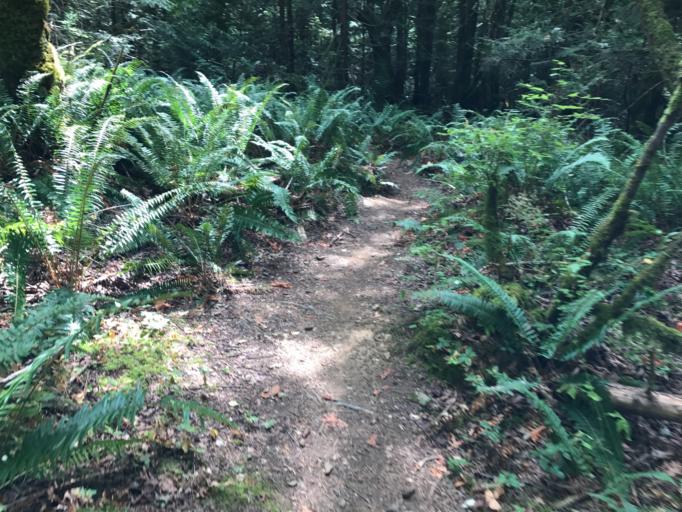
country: CA
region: British Columbia
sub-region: Cowichan Valley Regional District
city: Ladysmith
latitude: 48.9284
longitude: -123.7429
